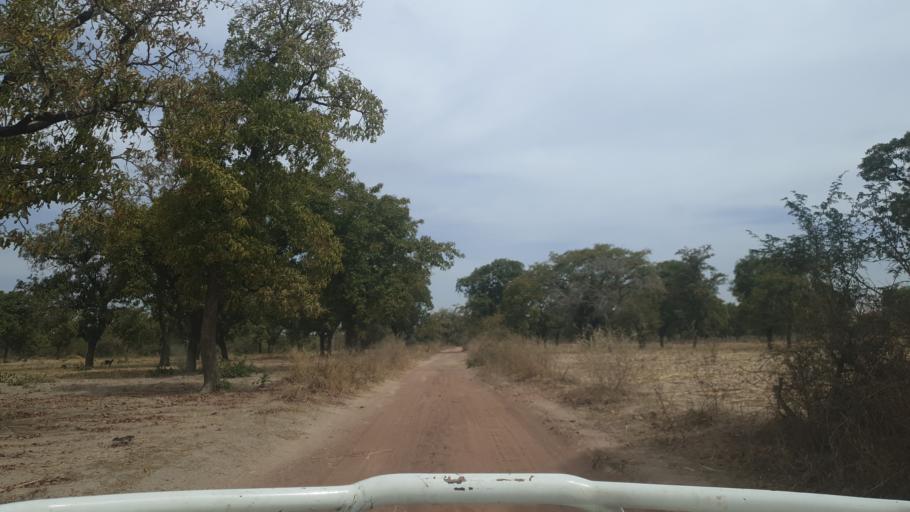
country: ML
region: Sikasso
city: Yorosso
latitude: 12.2331
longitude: -4.7468
